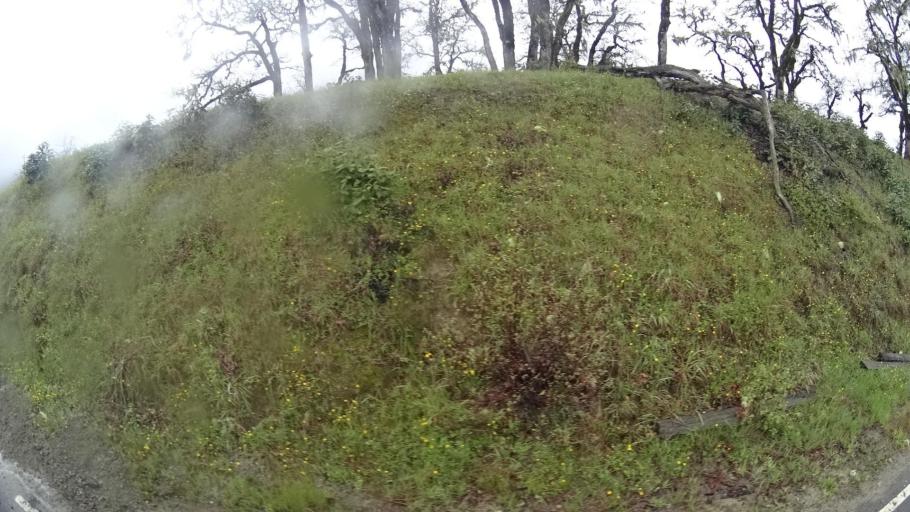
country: US
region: California
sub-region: Humboldt County
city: Westhaven-Moonstone
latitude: 41.1589
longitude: -123.8937
